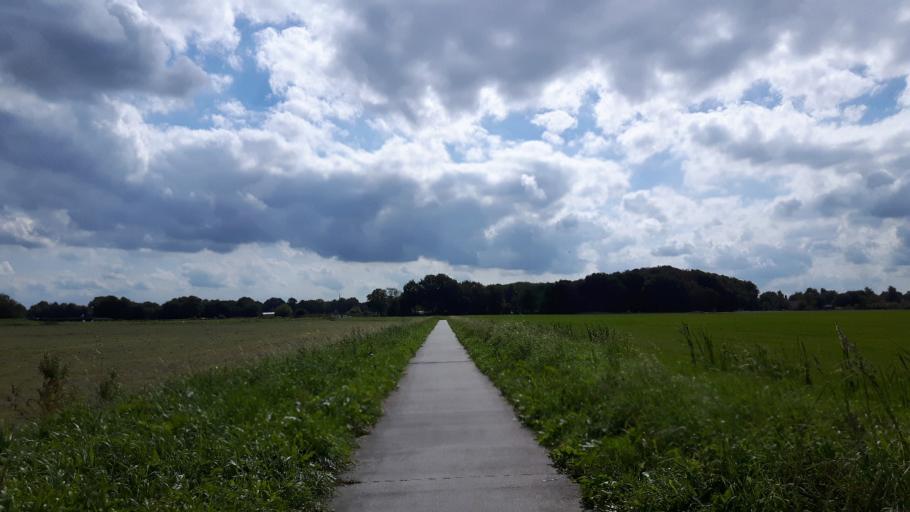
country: NL
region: Friesland
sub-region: Gemeente Heerenveen
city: Jubbega
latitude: 53.0046
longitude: 6.2916
